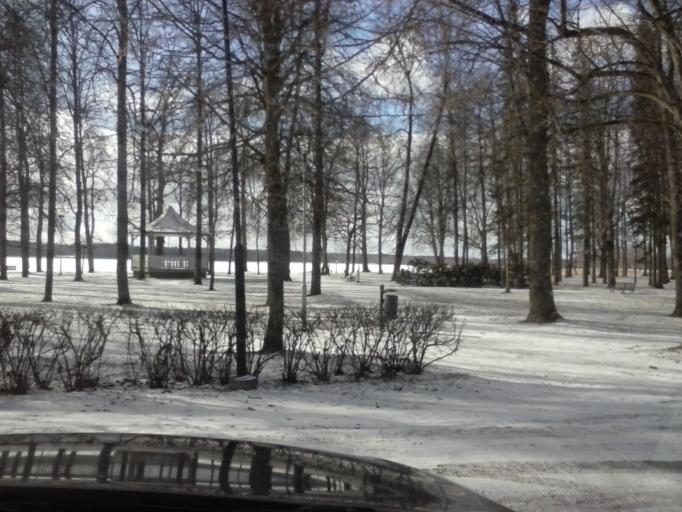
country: EE
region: Vorumaa
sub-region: Voru linn
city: Voru
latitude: 57.8452
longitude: 26.9901
